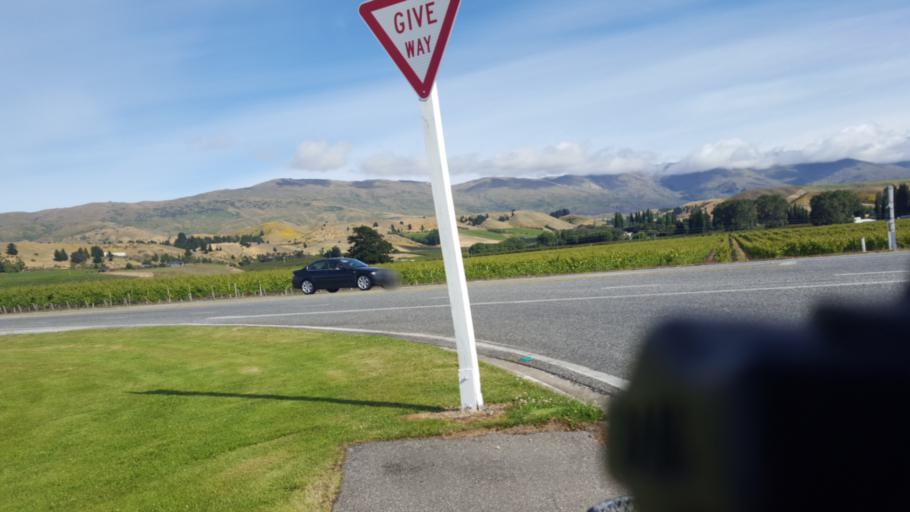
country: NZ
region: Otago
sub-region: Queenstown-Lakes District
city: Wanaka
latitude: -45.0351
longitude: 169.1994
